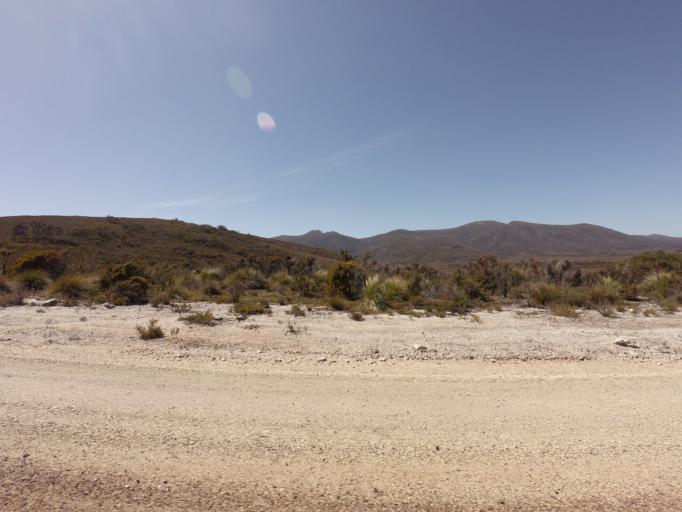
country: AU
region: Tasmania
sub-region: Huon Valley
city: Geeveston
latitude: -43.0343
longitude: 146.3336
